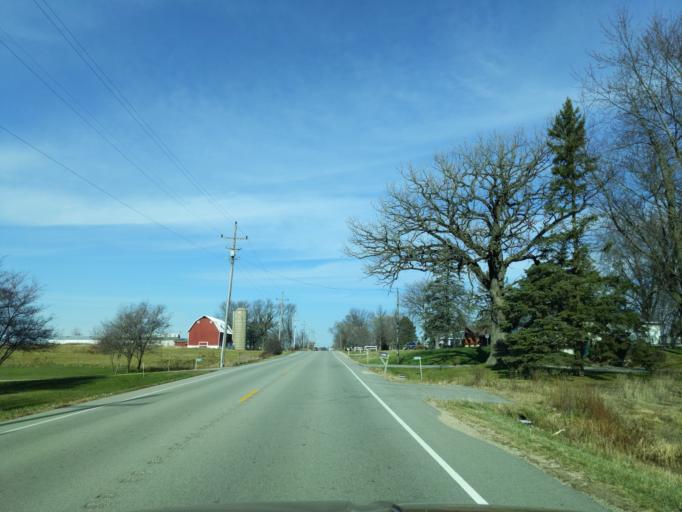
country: US
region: Wisconsin
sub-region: Walworth County
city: Elkhorn
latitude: 42.7138
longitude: -88.5817
